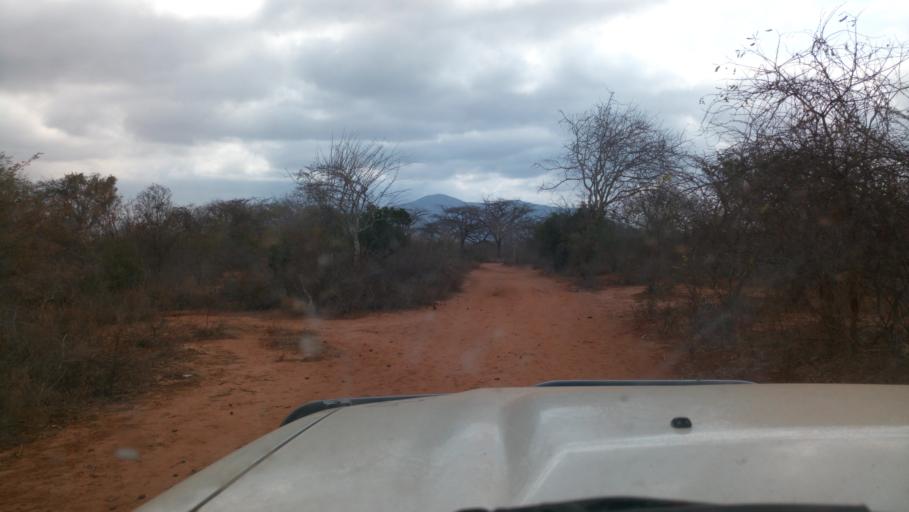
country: KE
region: Kitui
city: Kitui
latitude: -1.8396
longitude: 38.3415
